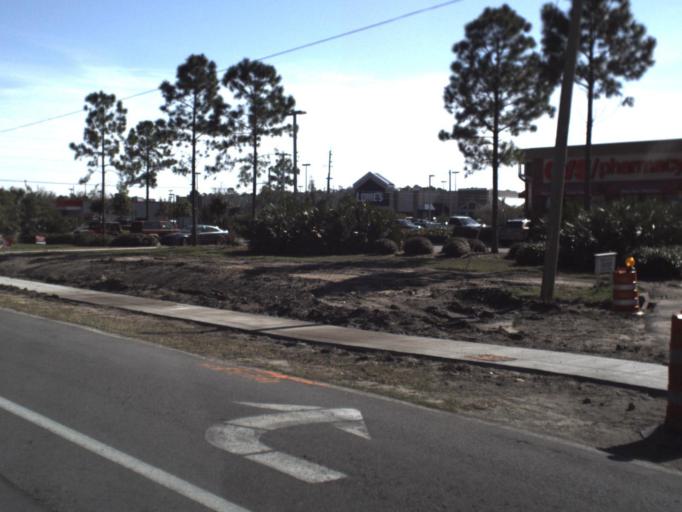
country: US
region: Florida
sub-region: Bay County
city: Panama City Beach
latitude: 30.2013
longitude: -85.8208
